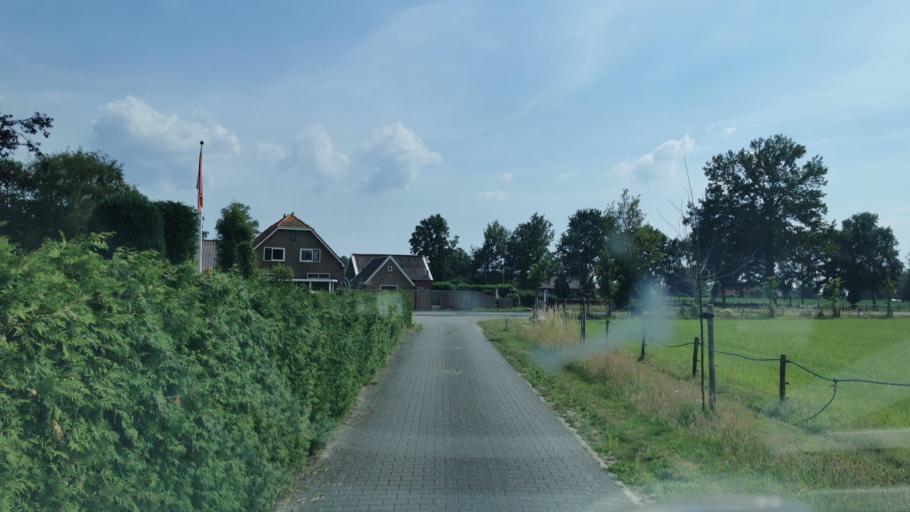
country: NL
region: Overijssel
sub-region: Gemeente Hengelo
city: Hengelo
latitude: 52.3061
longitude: 6.8550
